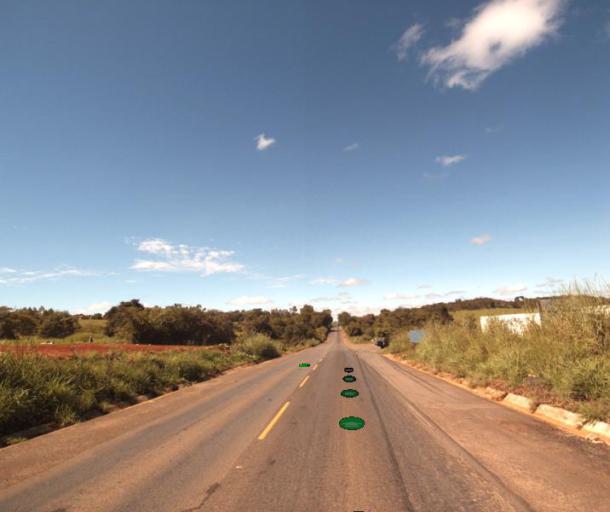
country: BR
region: Goias
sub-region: Rialma
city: Rialma
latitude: -15.3212
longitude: -49.5719
